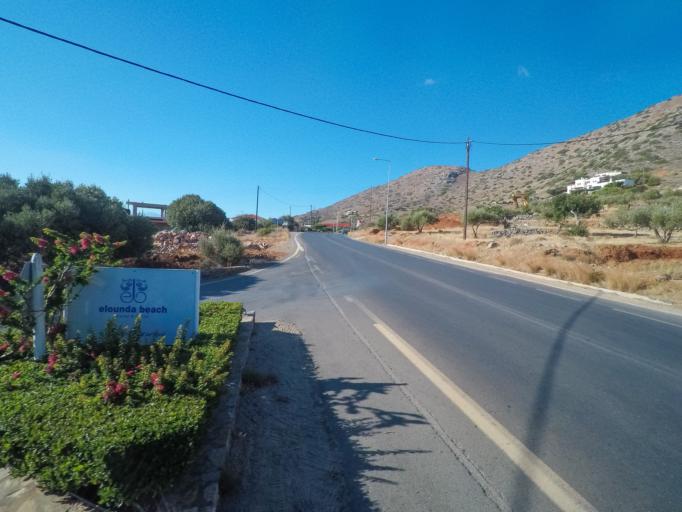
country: GR
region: Crete
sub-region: Nomos Lasithiou
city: Skhisma
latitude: 35.2449
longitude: 25.7256
